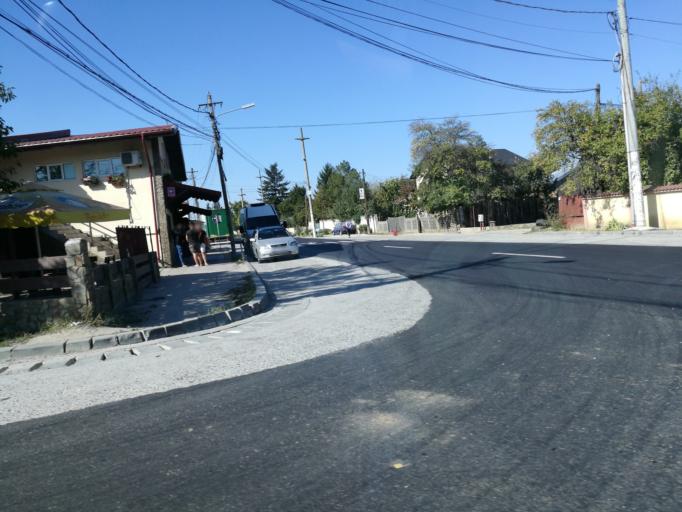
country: RO
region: Giurgiu
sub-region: Comuna Joita
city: Bacu
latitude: 44.4812
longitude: 25.8946
